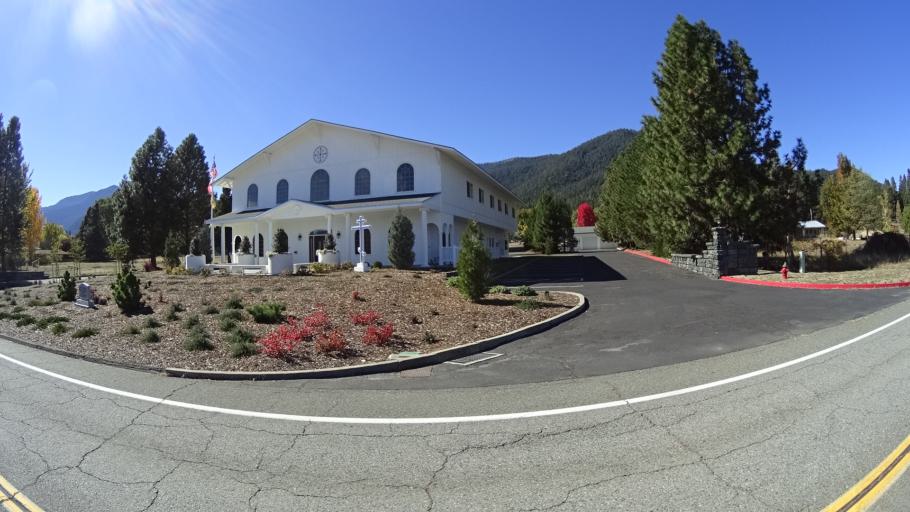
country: US
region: California
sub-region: Siskiyou County
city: Yreka
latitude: 41.4609
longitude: -122.8961
